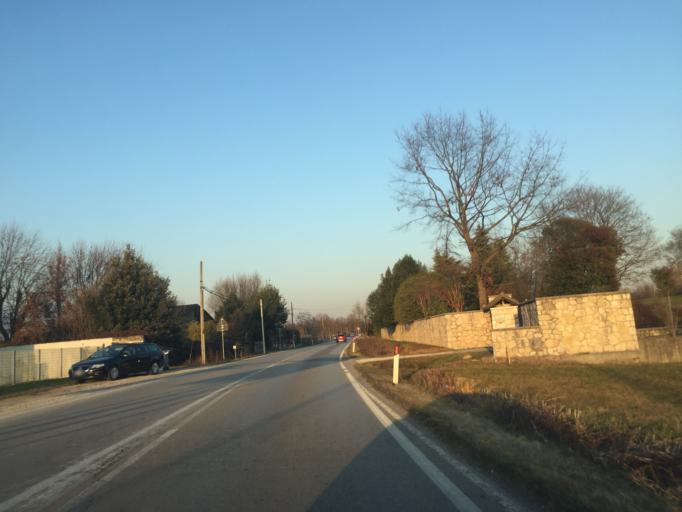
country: IT
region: Friuli Venezia Giulia
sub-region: Provincia di Pordenone
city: Vigonovo-Fontanafredda
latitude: 45.9790
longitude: 12.5302
